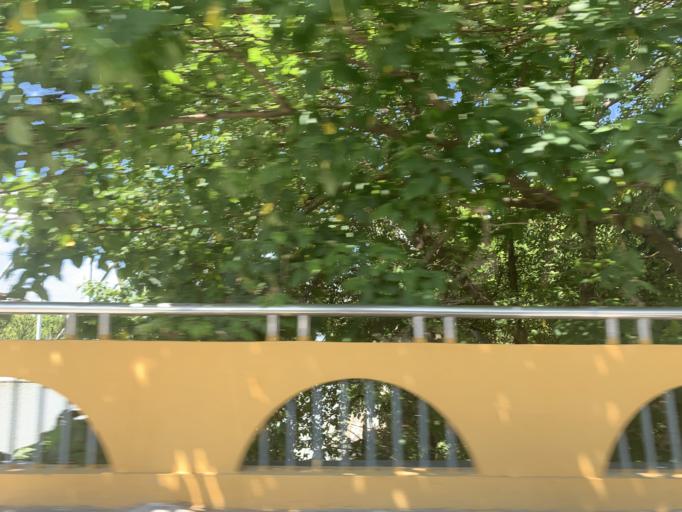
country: CN
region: Shanghai Shi
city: Huamu
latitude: 31.1763
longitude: 121.5347
